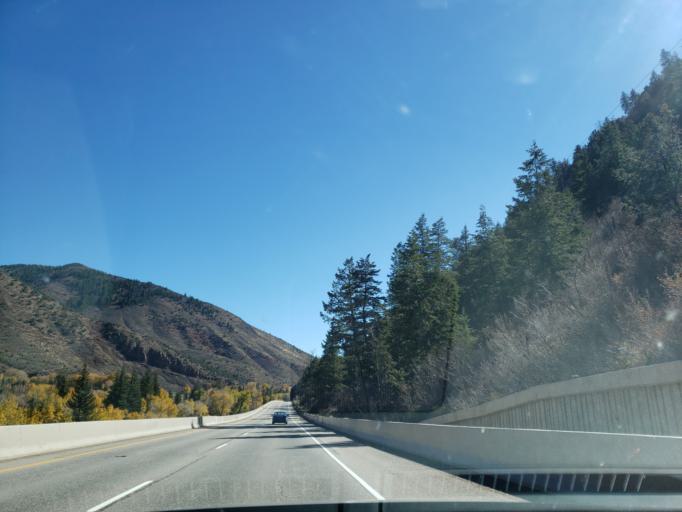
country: US
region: Colorado
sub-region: Eagle County
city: Basalt
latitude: 39.3202
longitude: -106.9450
